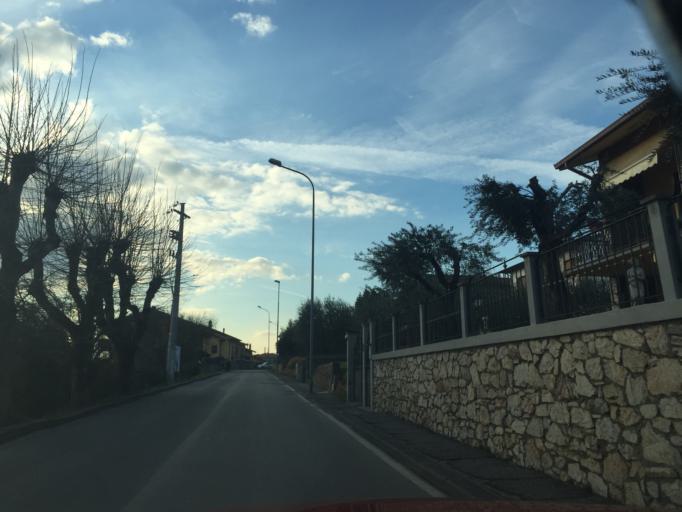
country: IT
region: Tuscany
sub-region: Provincia di Pistoia
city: Monsummano Terme
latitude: 43.8653
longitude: 10.8288
